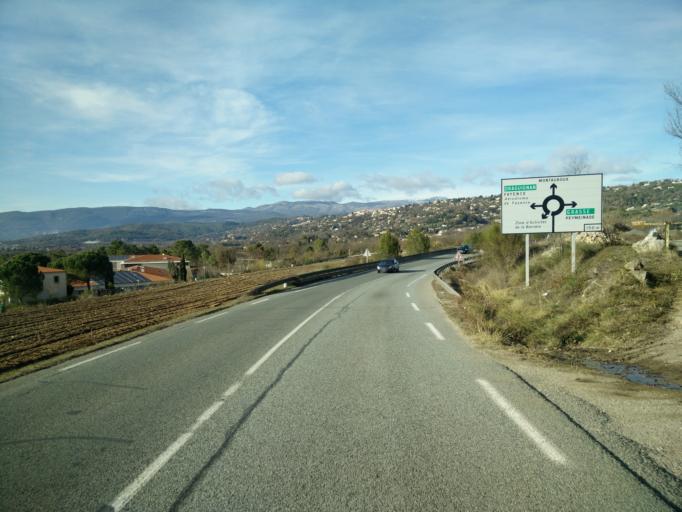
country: FR
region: Provence-Alpes-Cote d'Azur
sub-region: Departement du Var
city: Montauroux
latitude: 43.5974
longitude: 6.7867
